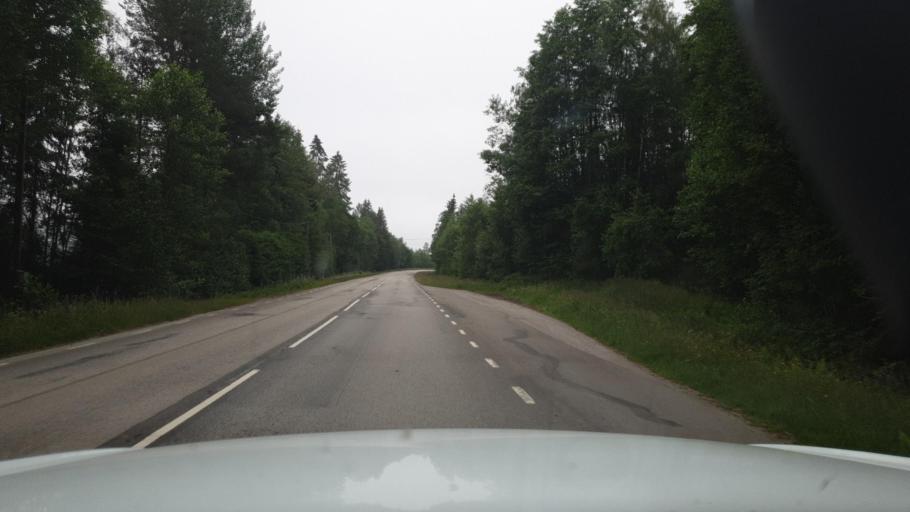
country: SE
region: Vaermland
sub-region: Arvika Kommun
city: Arvika
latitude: 59.7133
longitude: 12.6318
